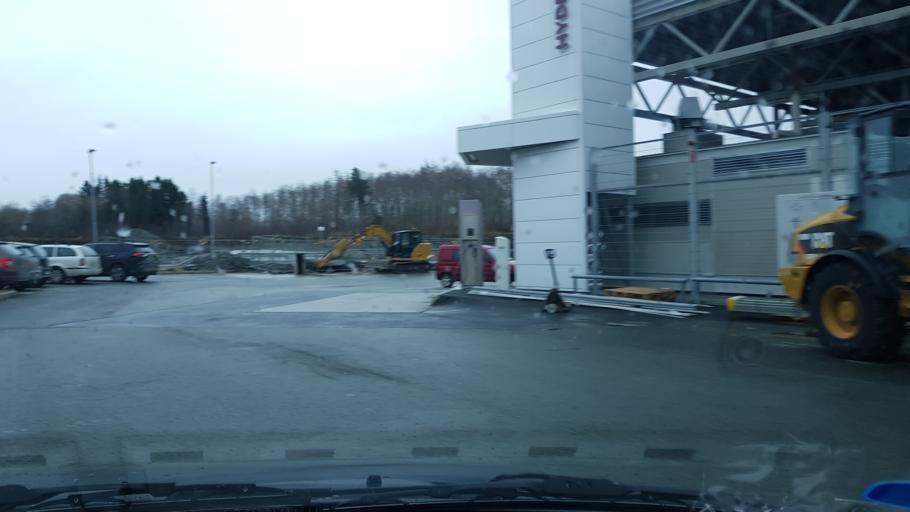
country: NO
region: Sor-Trondelag
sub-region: Trondheim
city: Trondheim
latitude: 63.3454
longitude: 10.3739
